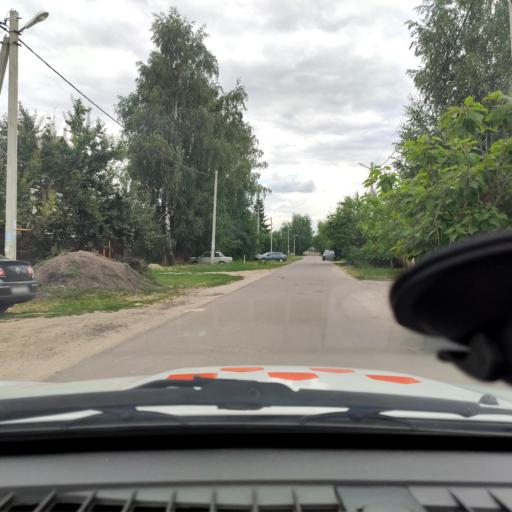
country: RU
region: Voronezj
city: Ramon'
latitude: 51.8275
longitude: 39.2585
